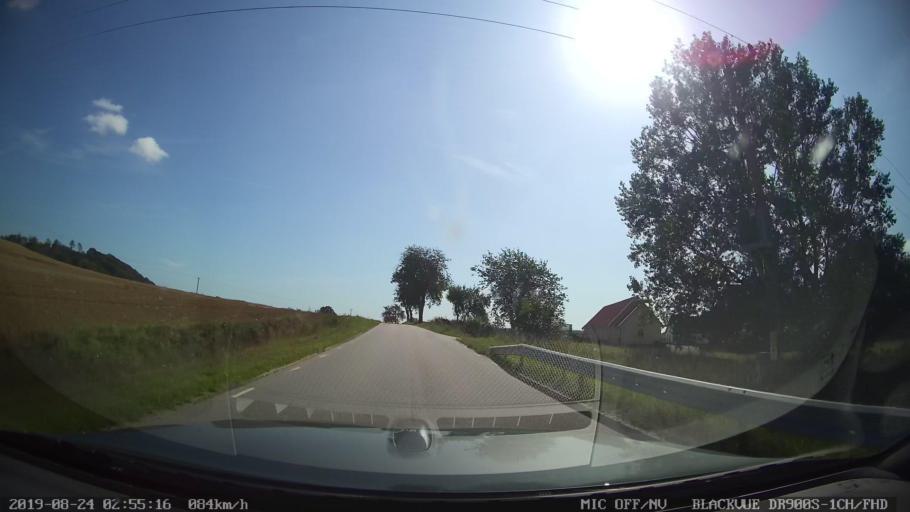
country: SE
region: Skane
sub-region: Trelleborgs Kommun
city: Anderslov
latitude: 55.4970
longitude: 13.3855
